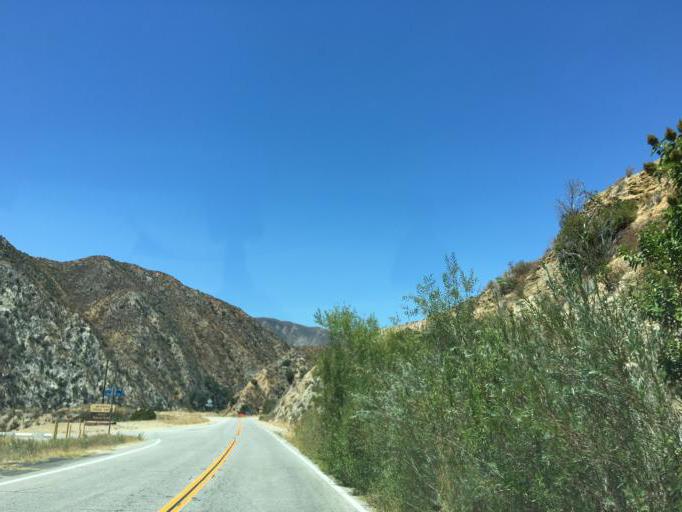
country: US
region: California
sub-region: Los Angeles County
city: La Crescenta-Montrose
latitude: 34.2976
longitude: -118.2430
